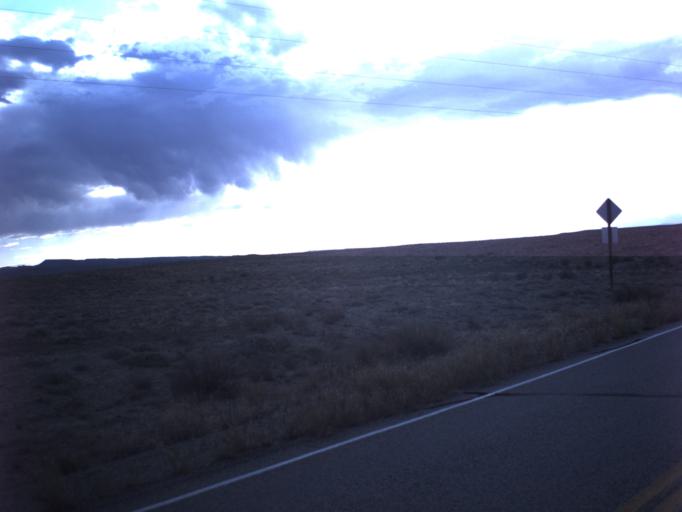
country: US
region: Utah
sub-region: Grand County
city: Moab
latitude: 38.9021
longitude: -109.3156
